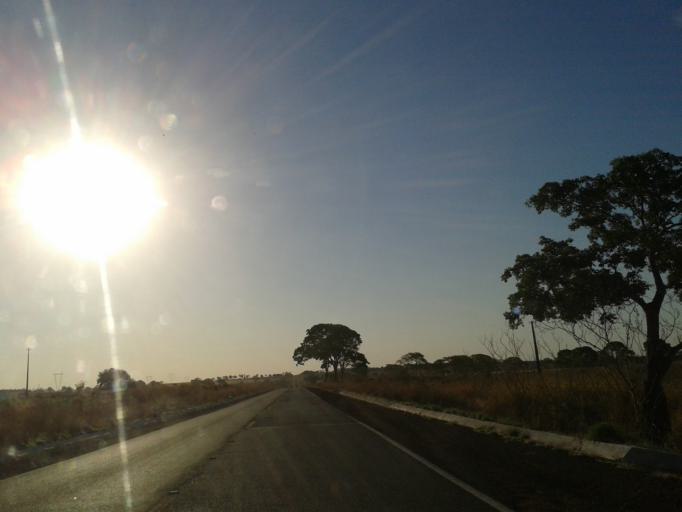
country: BR
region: Minas Gerais
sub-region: Santa Vitoria
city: Santa Vitoria
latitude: -19.1075
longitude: -50.3223
